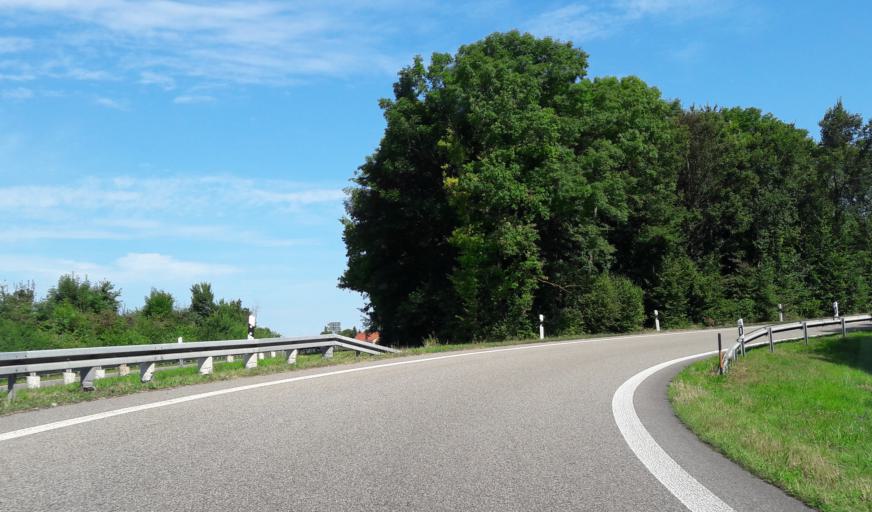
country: DE
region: Baden-Wuerttemberg
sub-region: Regierungsbezirk Stuttgart
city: Korntal
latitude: 48.8509
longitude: 9.1191
